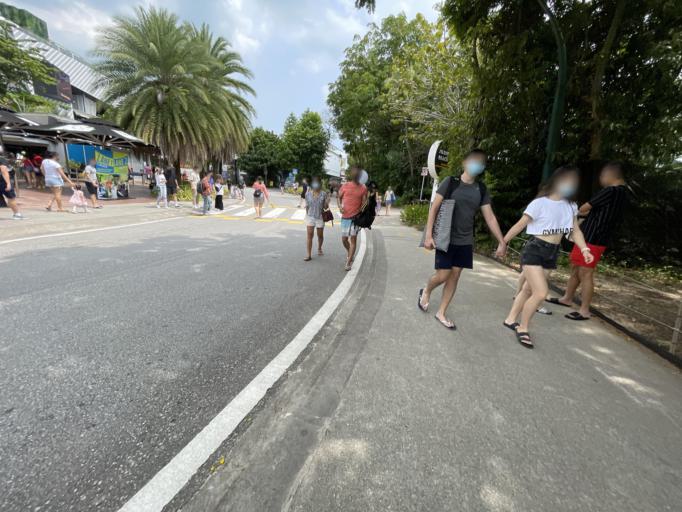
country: SG
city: Singapore
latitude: 1.2519
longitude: 103.8166
